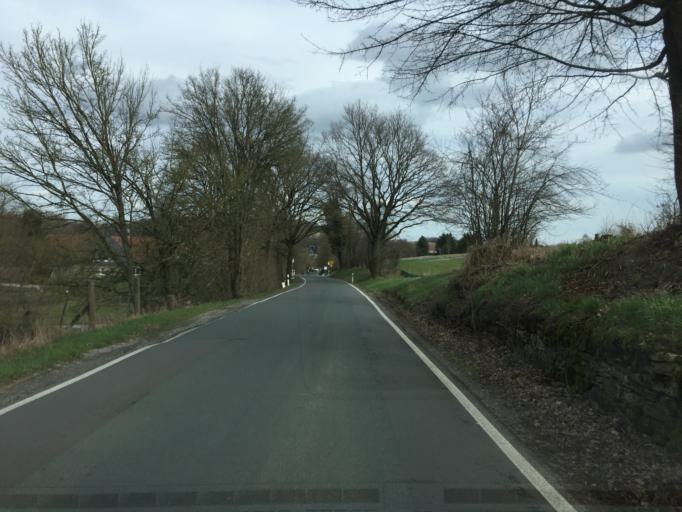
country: DE
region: North Rhine-Westphalia
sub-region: Regierungsbezirk Detmold
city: Detmold
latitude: 51.9057
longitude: 8.8653
